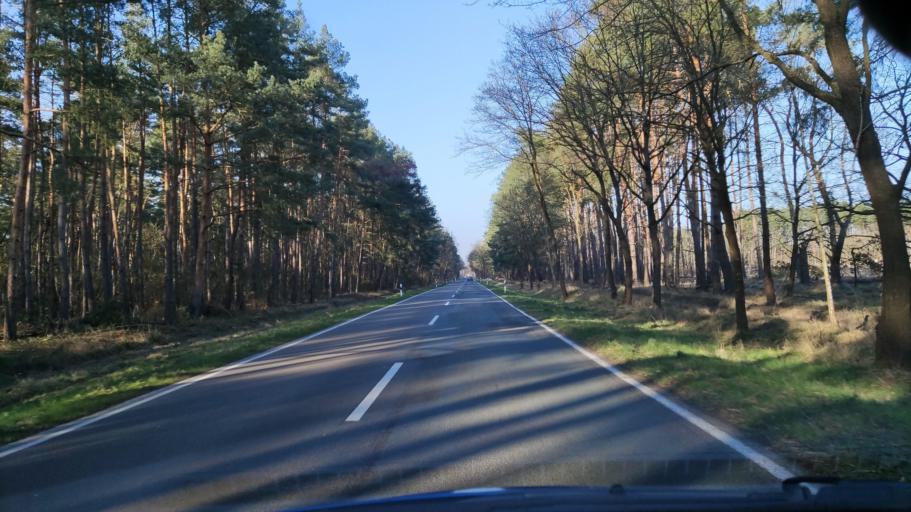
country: DE
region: Saxony-Anhalt
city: Seehausen
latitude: 52.8686
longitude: 11.7384
